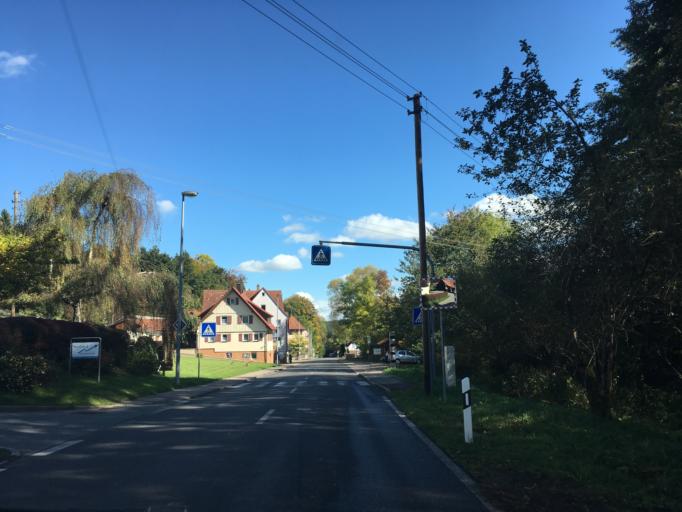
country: DE
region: Baden-Wuerttemberg
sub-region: Karlsruhe Region
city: Oberreichenbach
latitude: 48.7341
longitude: 8.6709
